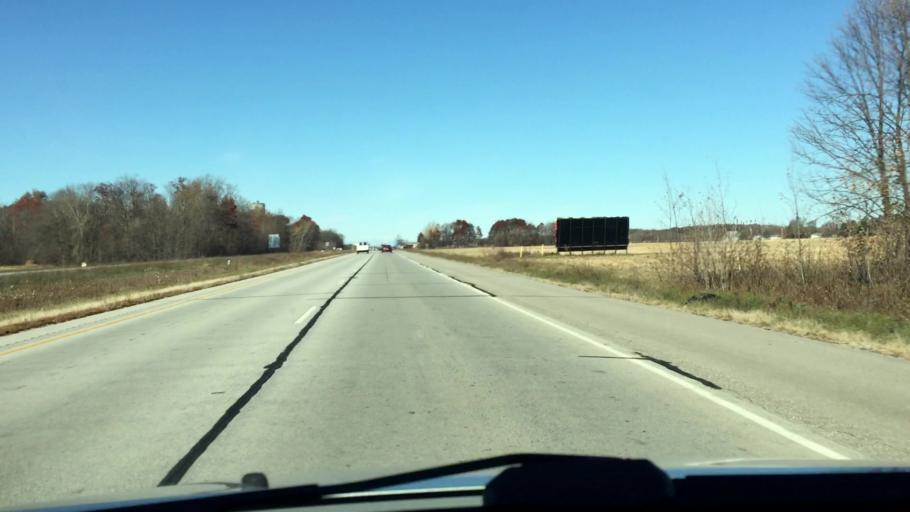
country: US
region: Wisconsin
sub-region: Brown County
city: Howard
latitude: 44.5682
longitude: -88.1492
